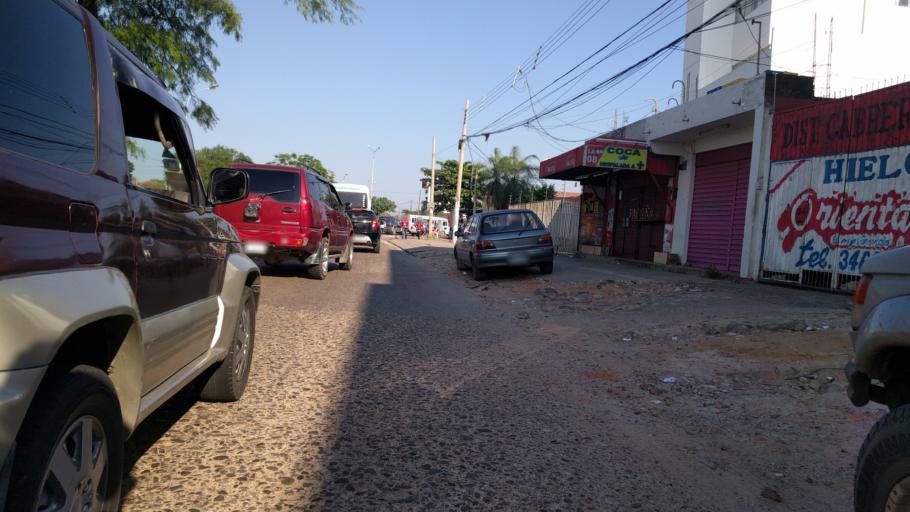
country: BO
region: Santa Cruz
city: Santa Cruz de la Sierra
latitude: -17.8226
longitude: -63.1829
